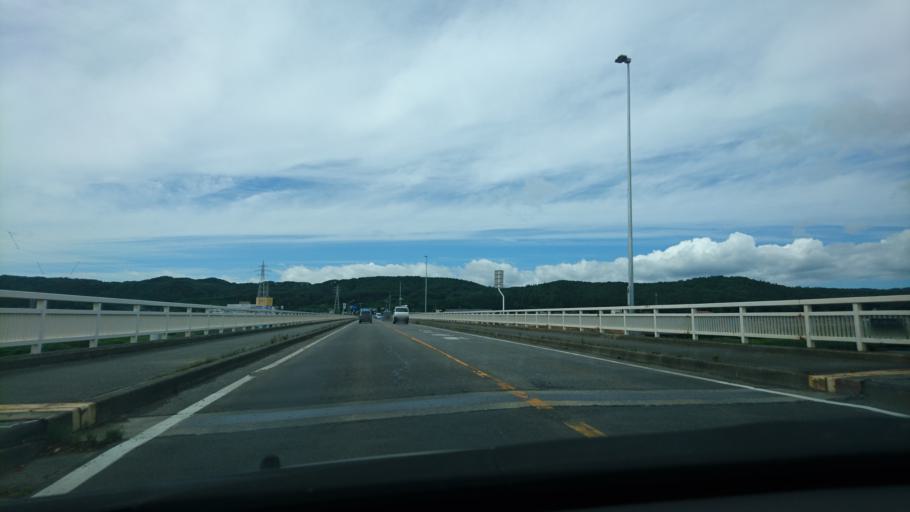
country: JP
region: Aomori
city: Hachinohe
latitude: 40.1928
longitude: 141.7853
